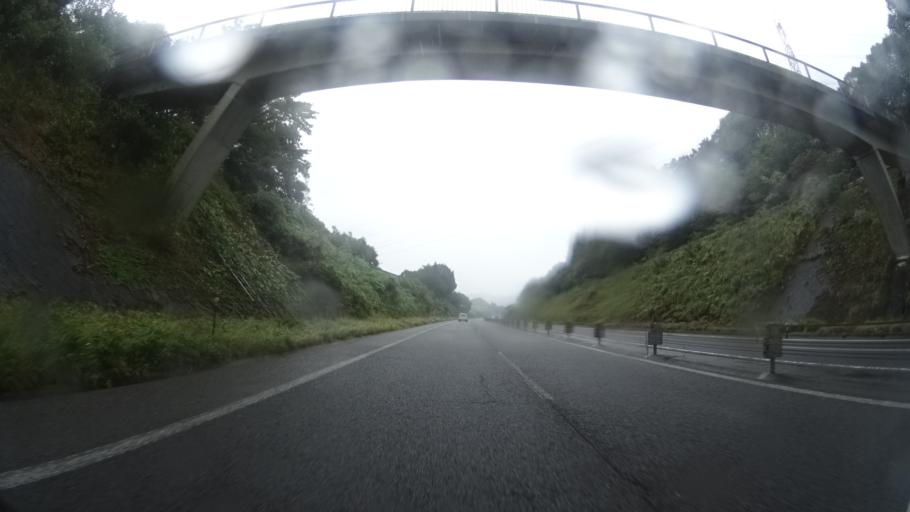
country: JP
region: Kagoshima
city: Okuchi-shinohara
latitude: 31.9280
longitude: 130.7043
